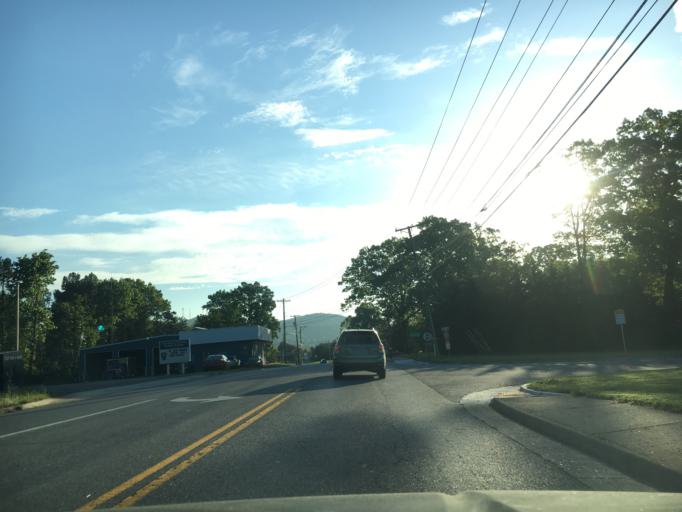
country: US
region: Virginia
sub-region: Campbell County
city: Rustburg
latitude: 37.2705
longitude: -79.1089
